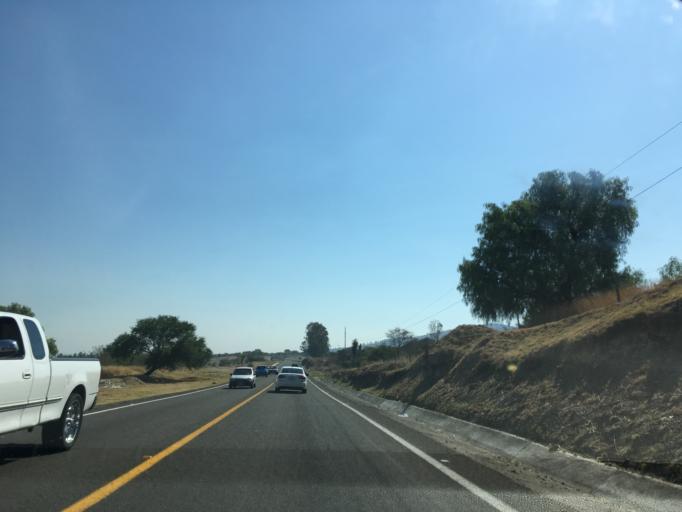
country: MX
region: Michoacan
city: Charo
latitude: 19.7598
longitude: -101.0339
